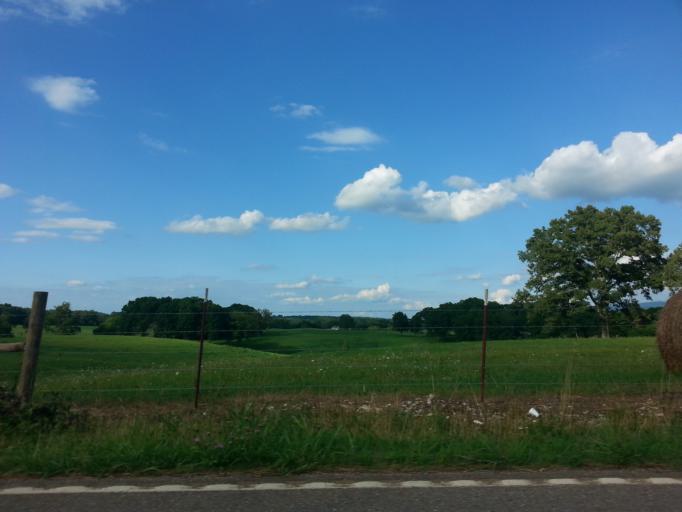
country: US
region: Tennessee
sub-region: Loudon County
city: Greenback
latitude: 35.6252
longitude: -84.0980
